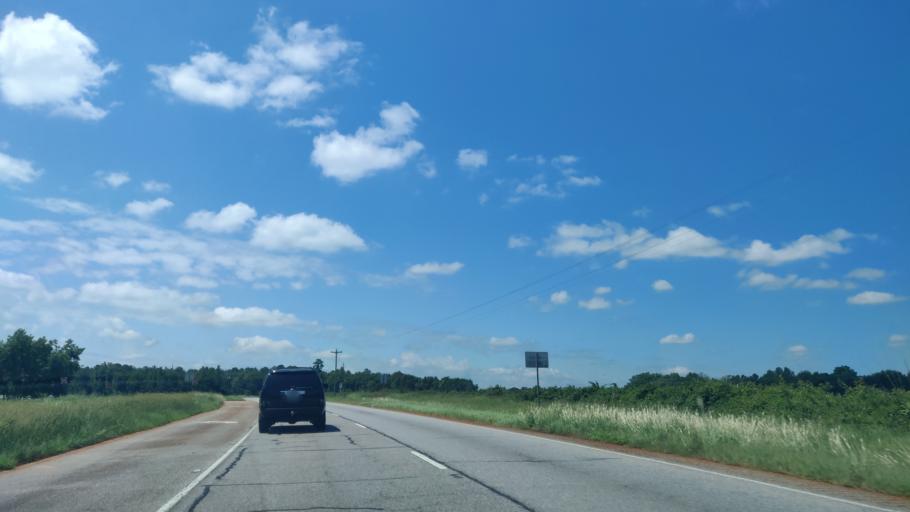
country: US
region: Georgia
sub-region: Stewart County
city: Richland
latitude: 32.0420
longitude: -84.6772
